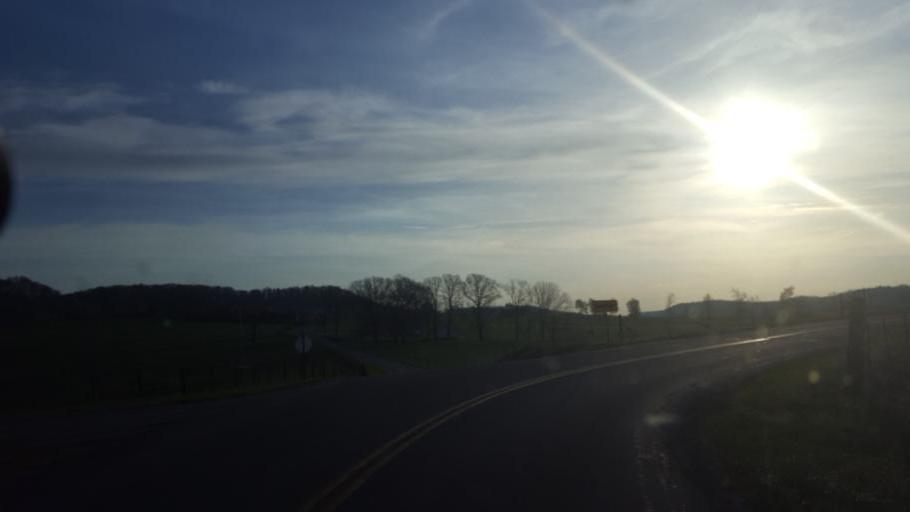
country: US
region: Kentucky
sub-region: Hart County
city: Horse Cave
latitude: 37.2213
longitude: -85.9513
